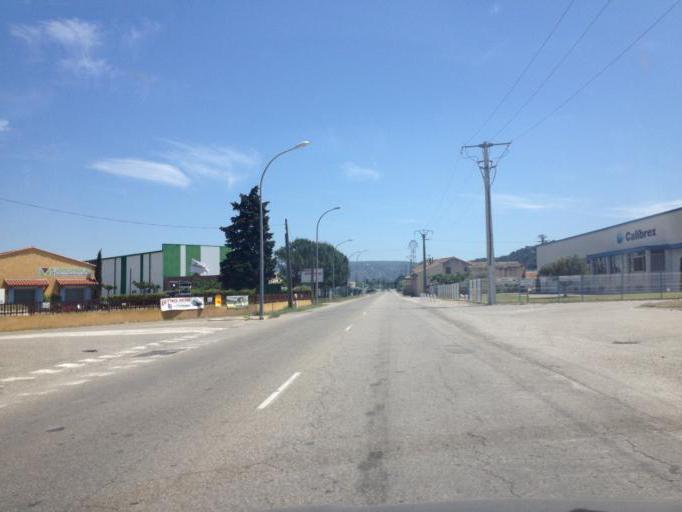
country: FR
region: Provence-Alpes-Cote d'Azur
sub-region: Departement du Vaucluse
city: Cavaillon
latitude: 43.8561
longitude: 5.0185
